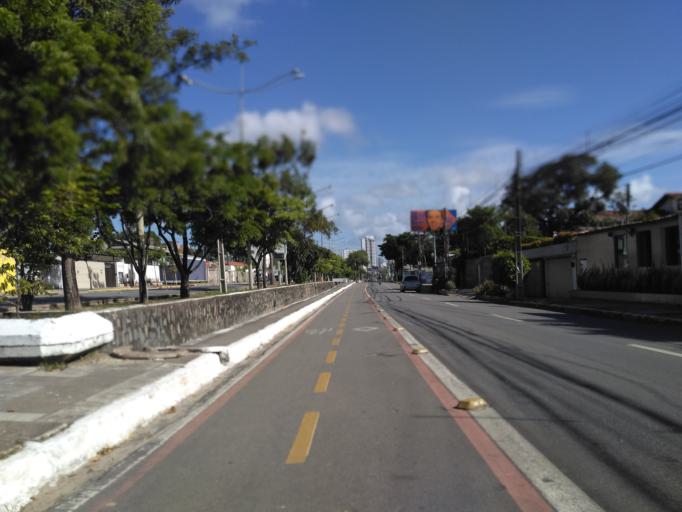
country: BR
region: Pernambuco
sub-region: Jaboatao Dos Guararapes
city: Jaboatao
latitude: -8.1617
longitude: -34.9142
